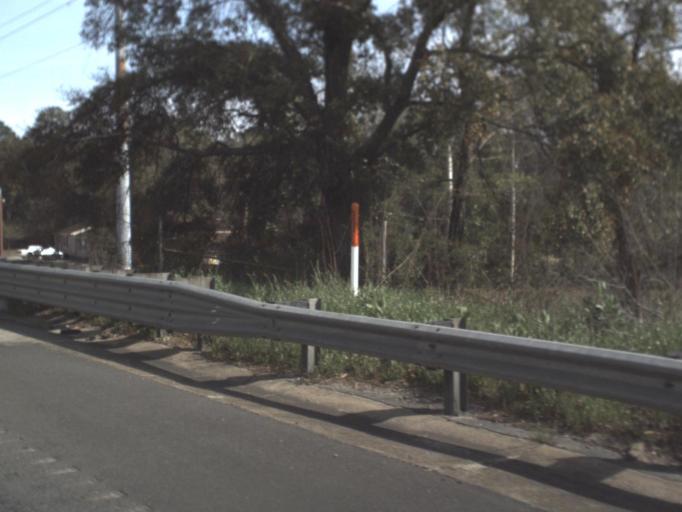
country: US
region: Florida
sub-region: Leon County
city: Tallahassee
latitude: 30.4781
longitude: -84.3449
